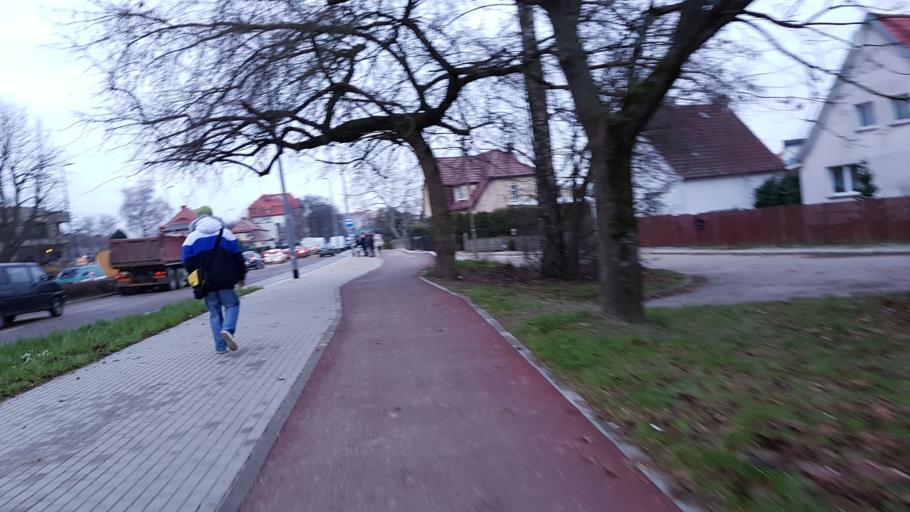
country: PL
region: West Pomeranian Voivodeship
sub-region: Koszalin
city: Koszalin
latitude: 54.1904
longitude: 16.2196
